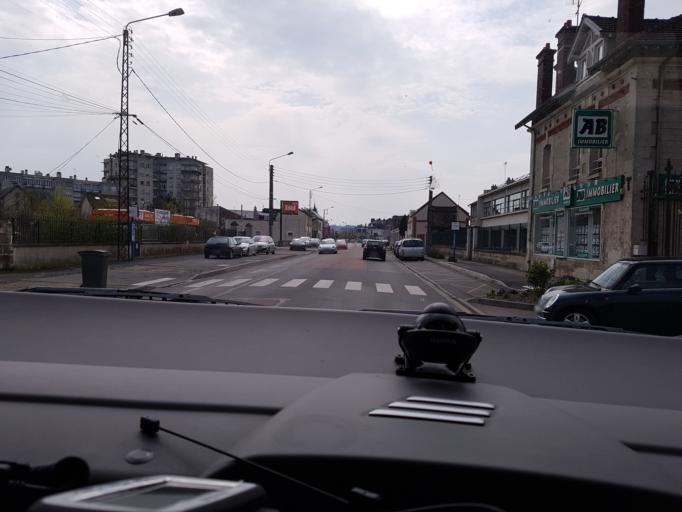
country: FR
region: Picardie
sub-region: Departement de l'Aisne
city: Soissons
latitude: 49.3881
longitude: 3.3329
